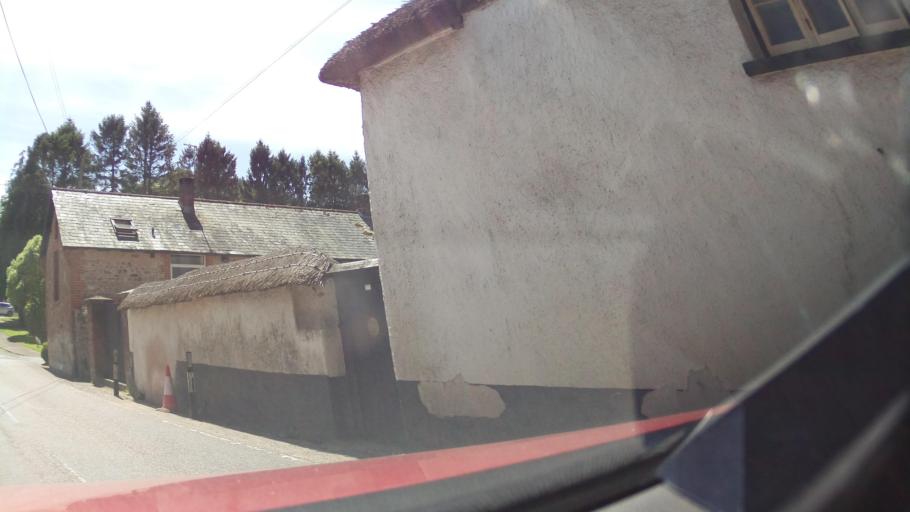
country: GB
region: England
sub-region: Devon
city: Sidmouth
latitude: 50.7032
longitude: -3.2655
